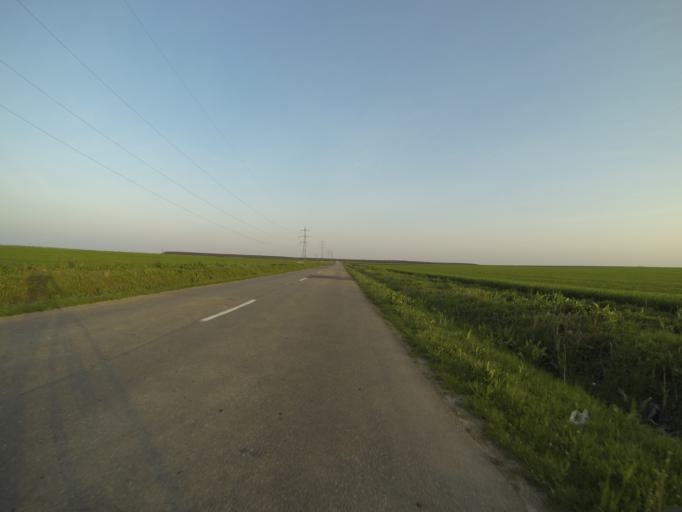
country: RO
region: Dolj
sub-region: Comuna Segarcea
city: Segarcea
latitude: 44.0774
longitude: 23.7905
